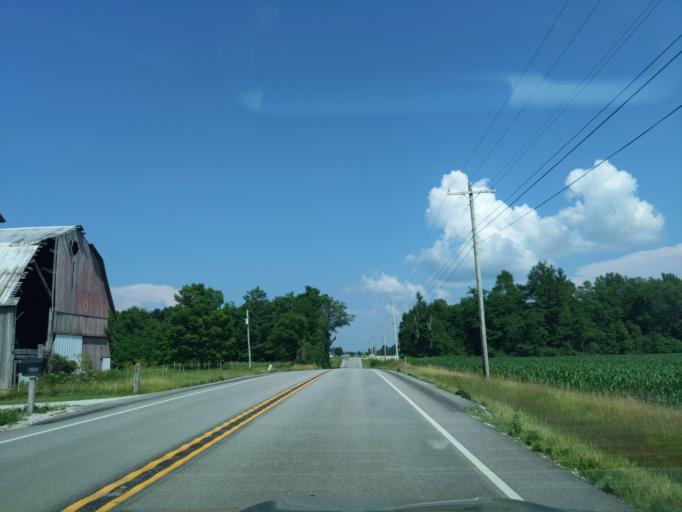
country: US
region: Indiana
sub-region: Ripley County
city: Osgood
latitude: 39.0749
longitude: -85.3608
